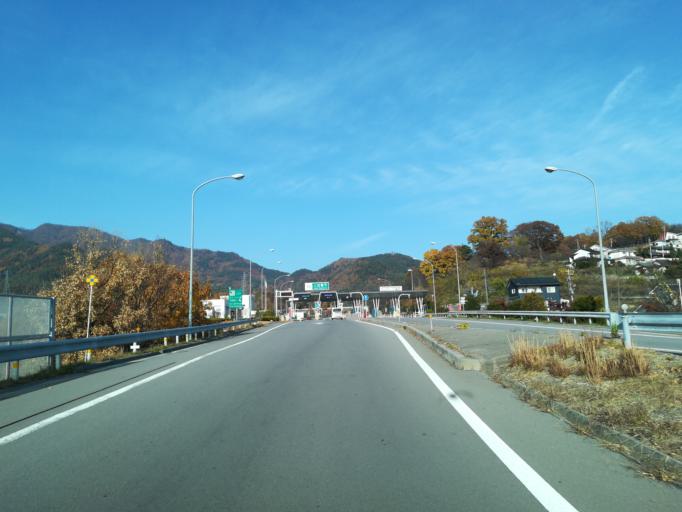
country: JP
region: Nagano
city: Ueda
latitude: 36.4094
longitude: 138.2804
